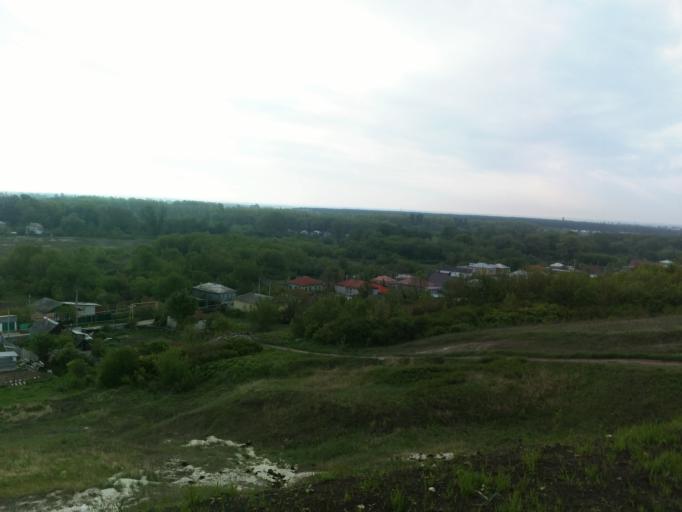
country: RU
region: Voronezj
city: Kalach
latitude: 50.4161
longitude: 41.0059
